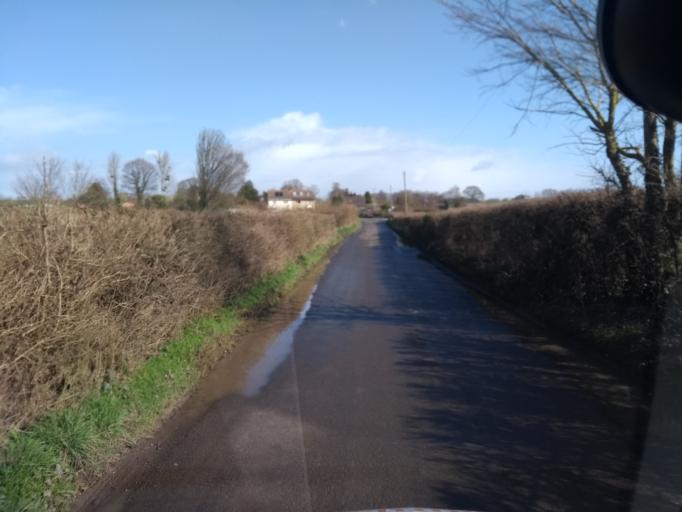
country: GB
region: England
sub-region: Somerset
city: South Petherton
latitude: 50.9614
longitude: -2.8372
